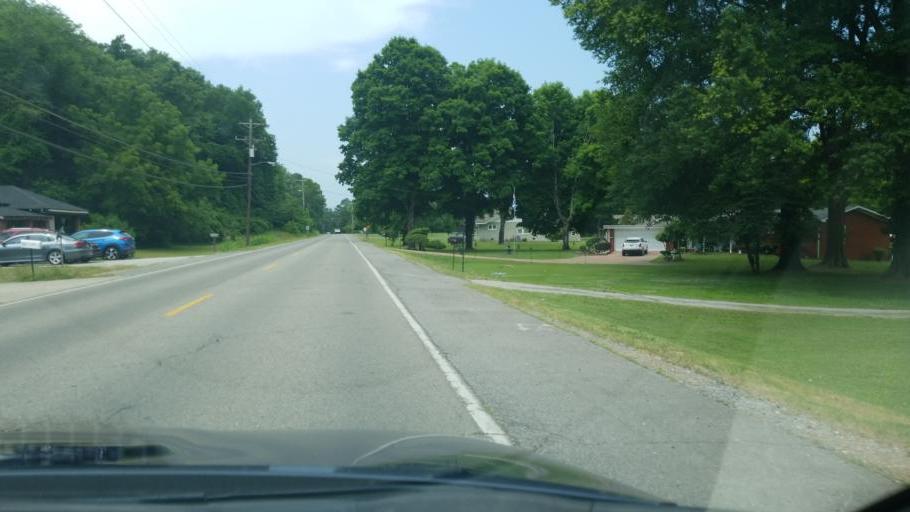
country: US
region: Tennessee
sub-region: Humphreys County
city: Waverly
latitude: 36.0826
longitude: -87.8159
